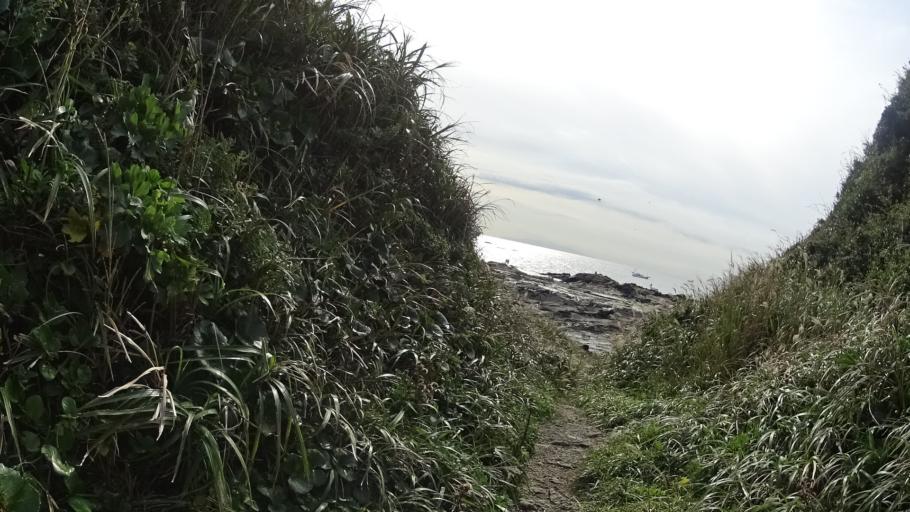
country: JP
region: Kanagawa
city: Miura
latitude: 35.1406
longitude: 139.6707
